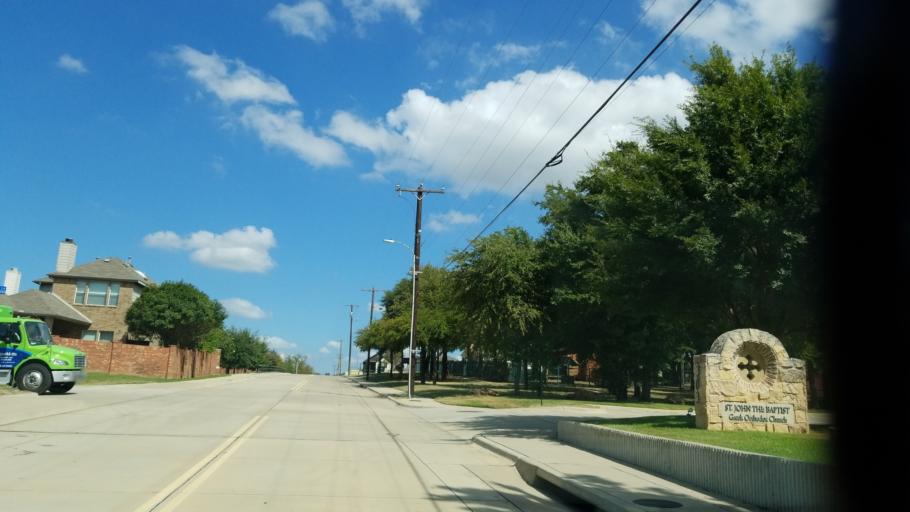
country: US
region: Texas
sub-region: Tarrant County
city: Euless
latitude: 32.8341
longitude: -97.0794
